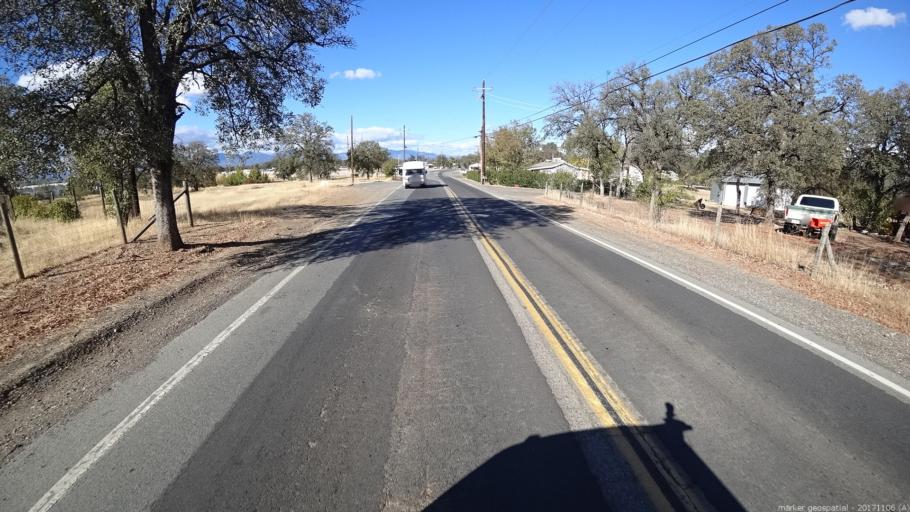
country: US
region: California
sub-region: Shasta County
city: Palo Cedro
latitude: 40.5773
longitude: -122.3048
